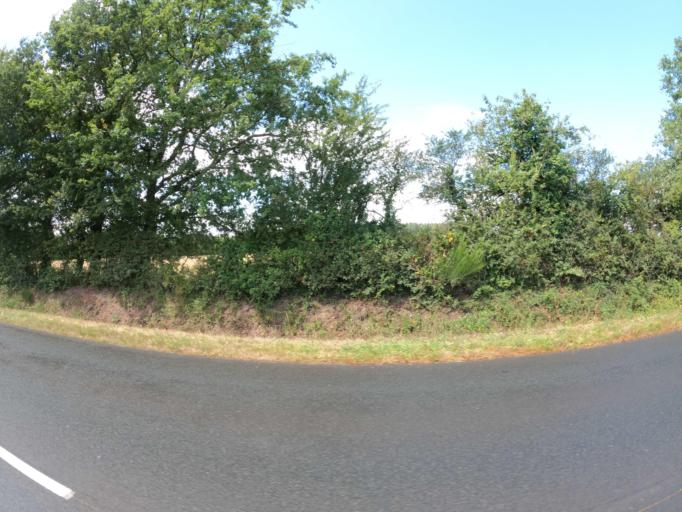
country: FR
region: Pays de la Loire
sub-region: Departement de Maine-et-Loire
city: Feneu
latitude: 47.6044
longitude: -0.5868
